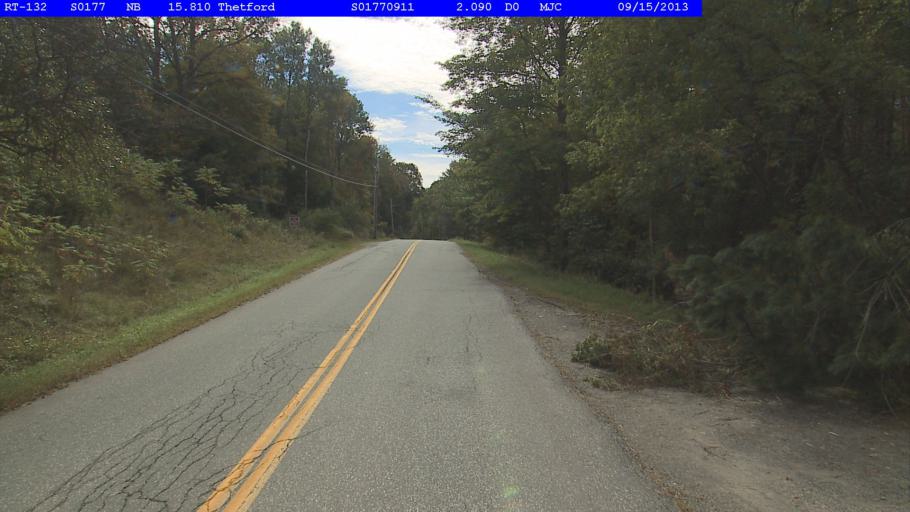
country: US
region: New Hampshire
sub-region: Grafton County
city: Hanover
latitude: 43.8251
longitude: -72.2858
